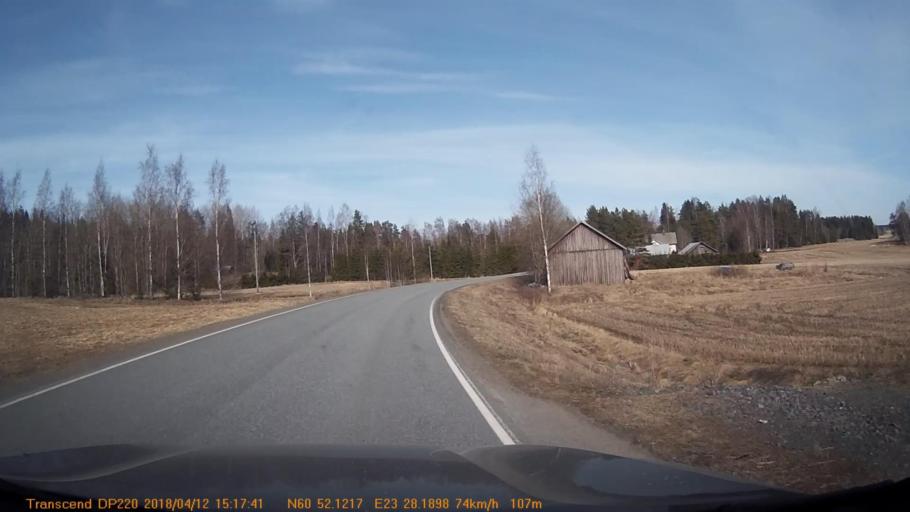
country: FI
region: Haeme
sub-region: Forssa
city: Jokioinen
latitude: 60.8689
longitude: 23.4704
